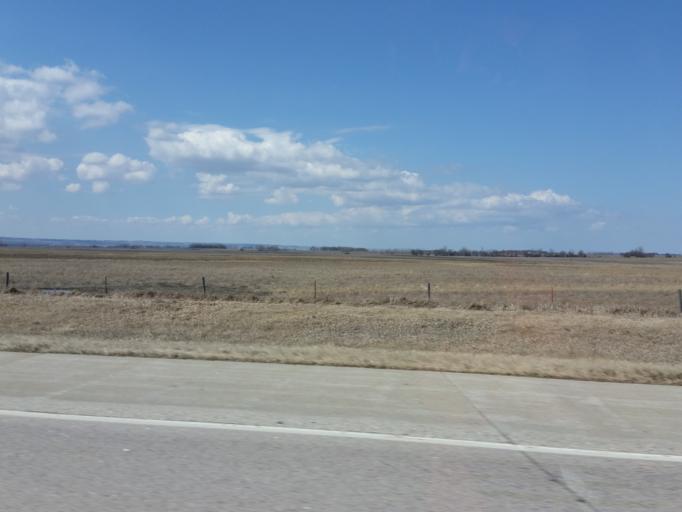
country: US
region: South Dakota
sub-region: Roberts County
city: Sisseton
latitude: 45.7158
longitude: -96.9535
